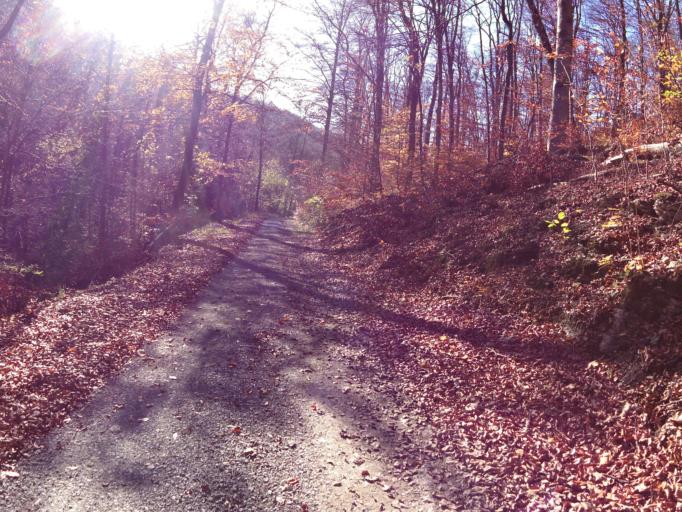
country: DE
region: Thuringia
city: Kammerforst
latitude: 51.0677
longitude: 10.4257
